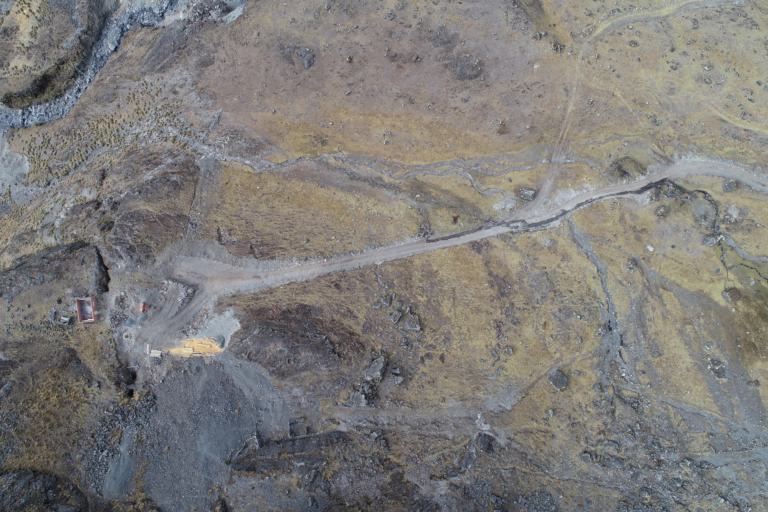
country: BO
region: La Paz
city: Sorata
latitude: -15.6696
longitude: -68.5517
